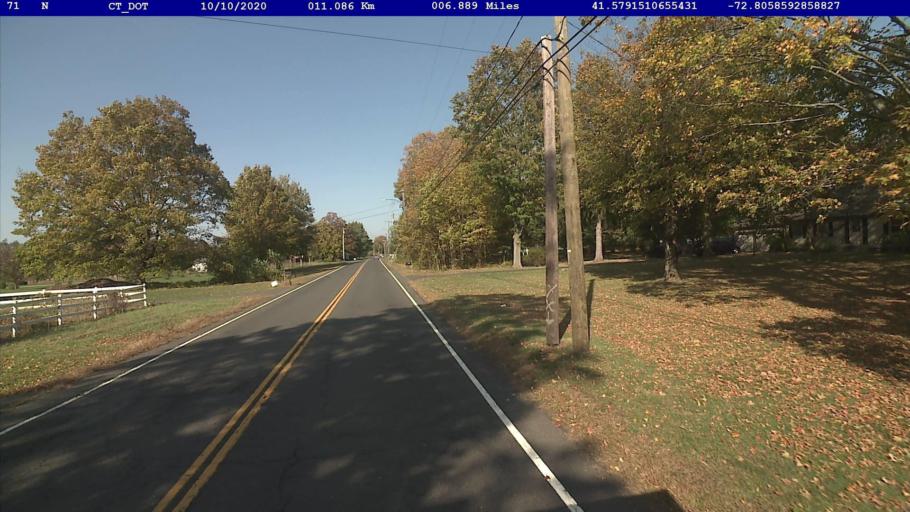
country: US
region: Connecticut
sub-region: New Haven County
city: Meriden
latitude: 41.5791
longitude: -72.8058
